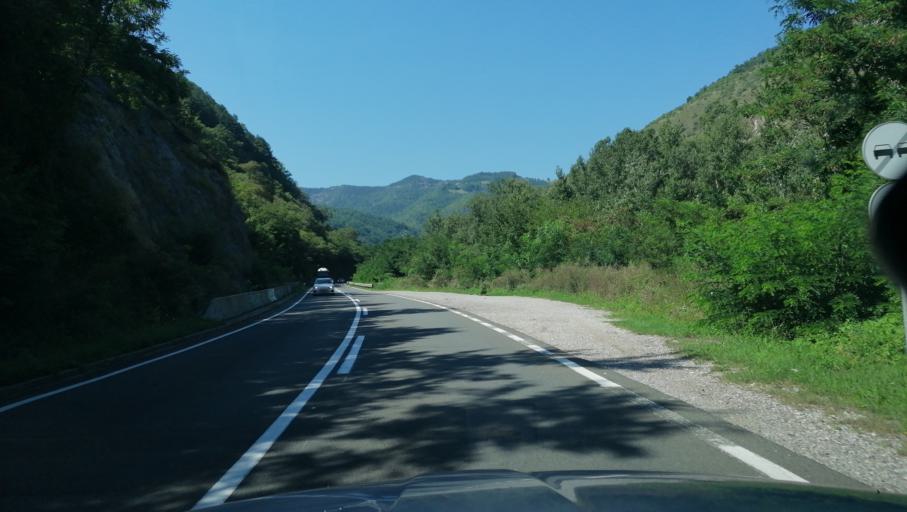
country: RS
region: Central Serbia
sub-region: Raski Okrug
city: Kraljevo
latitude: 43.6195
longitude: 20.5534
